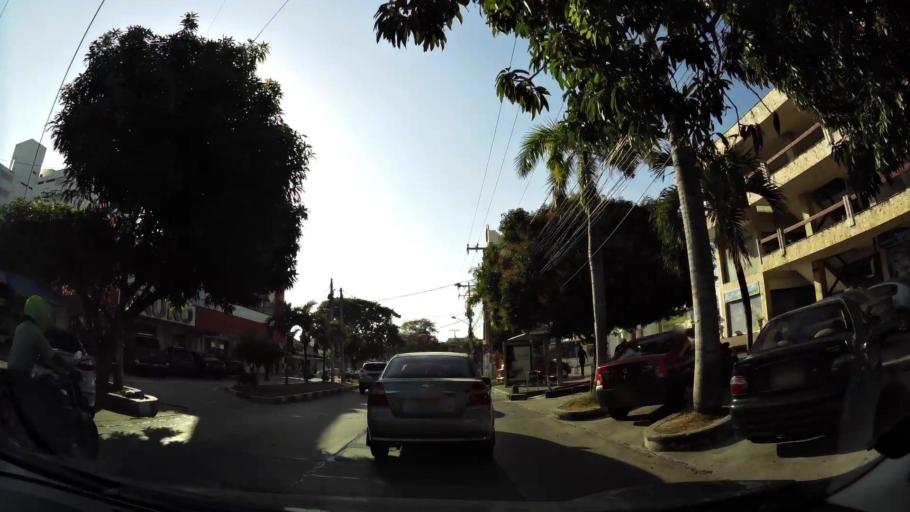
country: CO
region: Atlantico
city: Barranquilla
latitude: 10.9984
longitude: -74.8037
